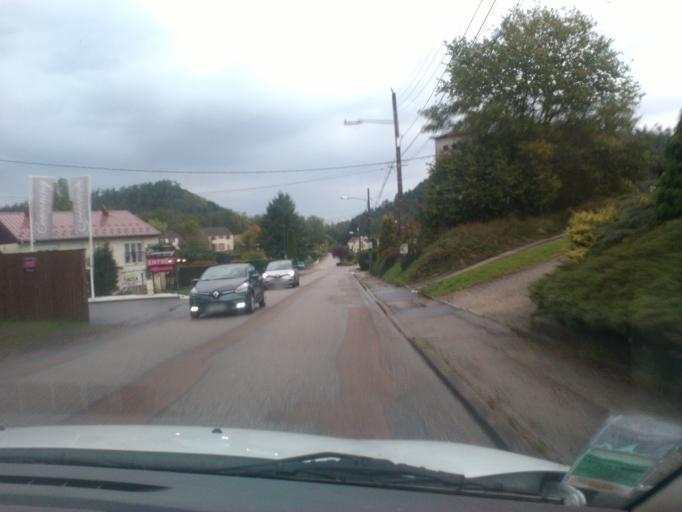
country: FR
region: Lorraine
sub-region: Departement des Vosges
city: Bruyeres
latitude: 48.2149
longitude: 6.7212
